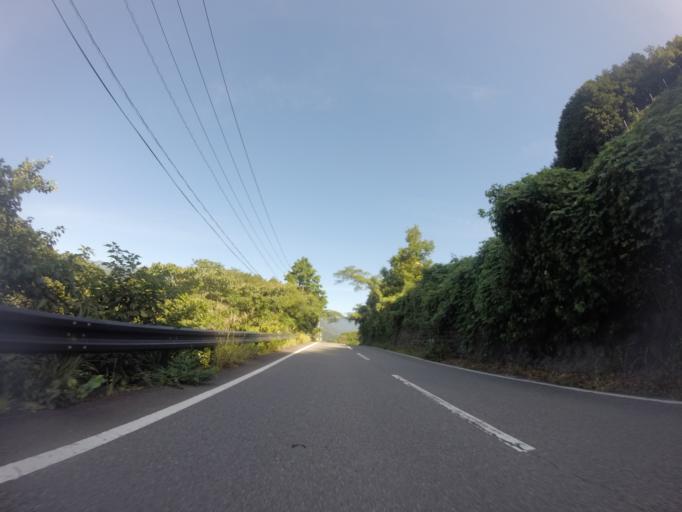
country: JP
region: Shizuoka
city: Fujinomiya
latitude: 35.3170
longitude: 138.4544
